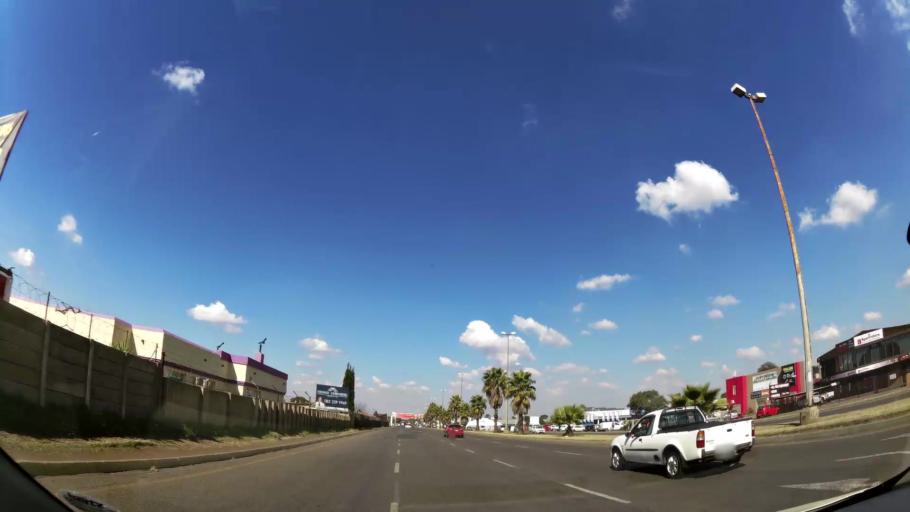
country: ZA
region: Mpumalanga
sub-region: Nkangala District Municipality
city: Witbank
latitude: -25.8966
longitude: 29.2305
